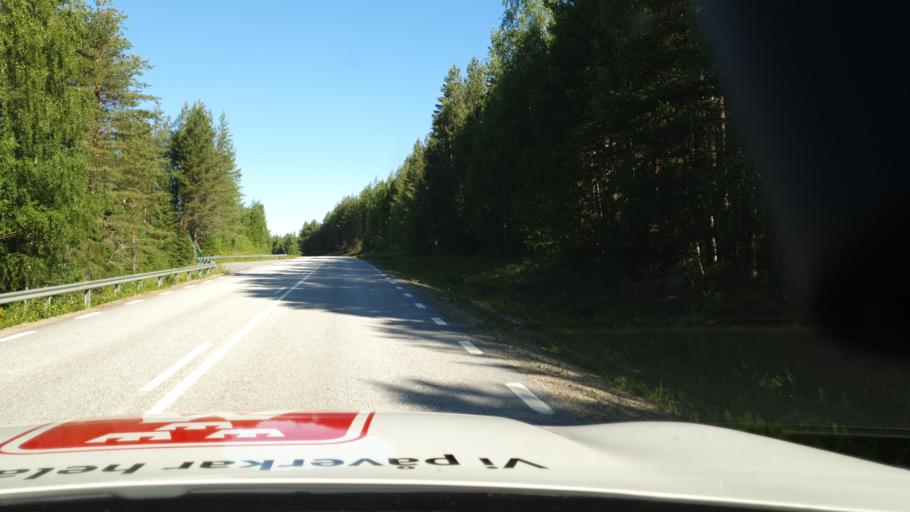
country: SE
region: Vaesterbotten
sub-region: Vindelns Kommun
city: Vindeln
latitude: 64.3573
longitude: 19.4543
